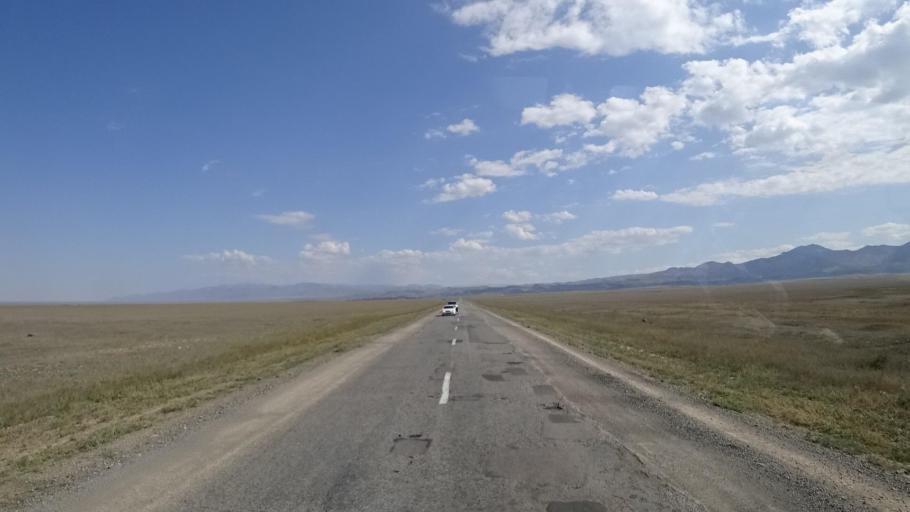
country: KZ
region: Almaty Oblysy
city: Kegen
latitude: 43.2258
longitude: 79.0465
